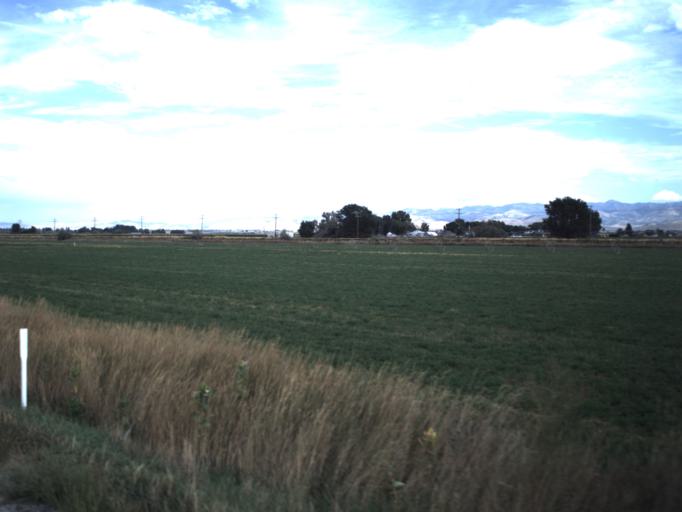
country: US
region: Utah
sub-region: Cache County
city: Lewiston
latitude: 41.9697
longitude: -111.9541
